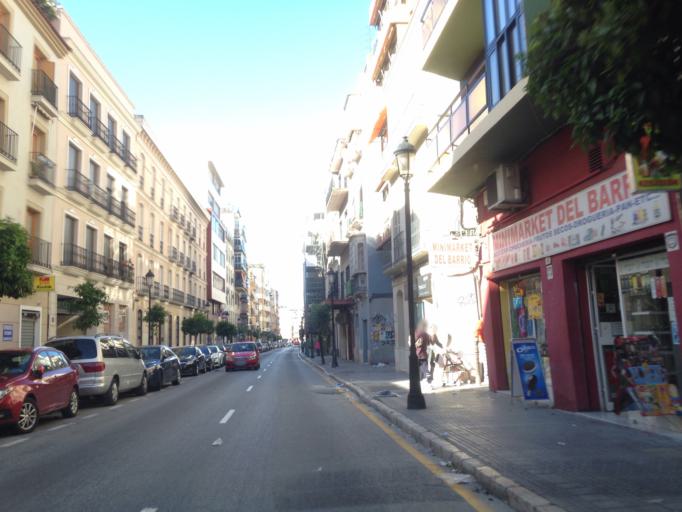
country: ES
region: Andalusia
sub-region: Provincia de Malaga
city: Malaga
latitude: 36.7259
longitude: -4.4146
